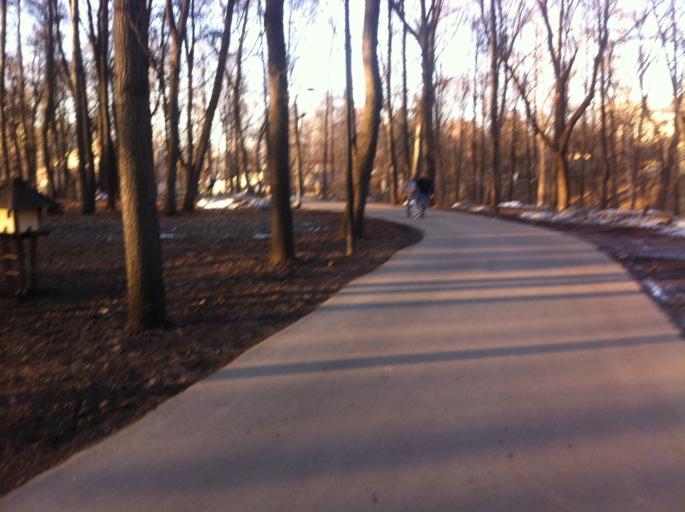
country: RU
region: Moscow
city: Novyye Cheremushki
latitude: 55.7191
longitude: 37.5909
